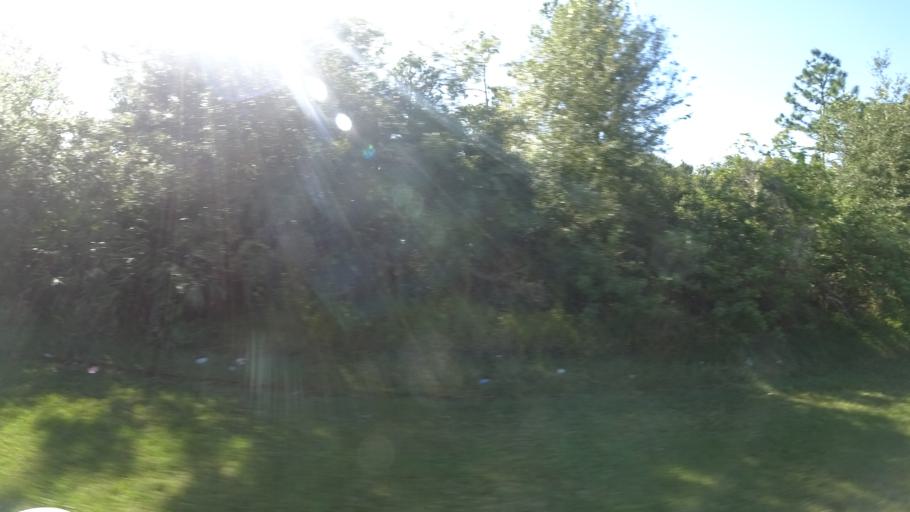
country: US
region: Florida
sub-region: Sarasota County
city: Fruitville
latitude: 27.4105
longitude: -82.2710
